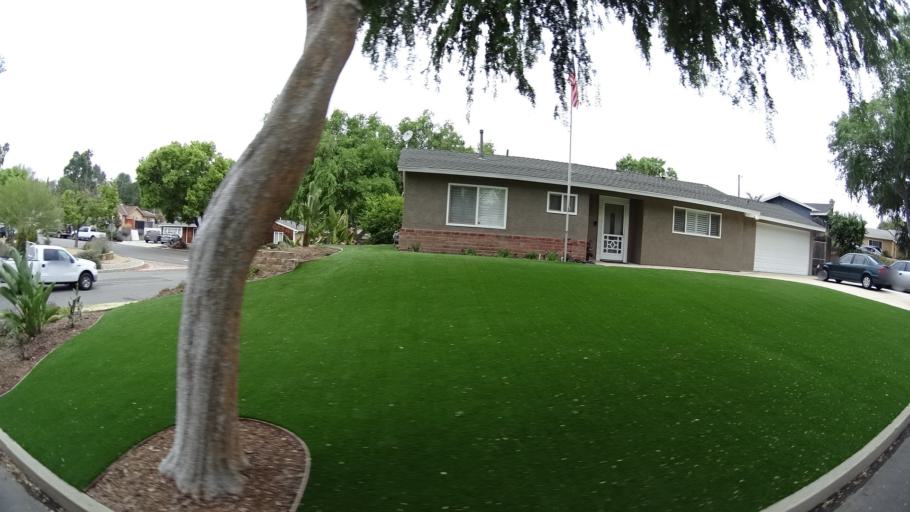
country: US
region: California
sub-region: Ventura County
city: Thousand Oaks
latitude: 34.2088
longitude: -118.8568
